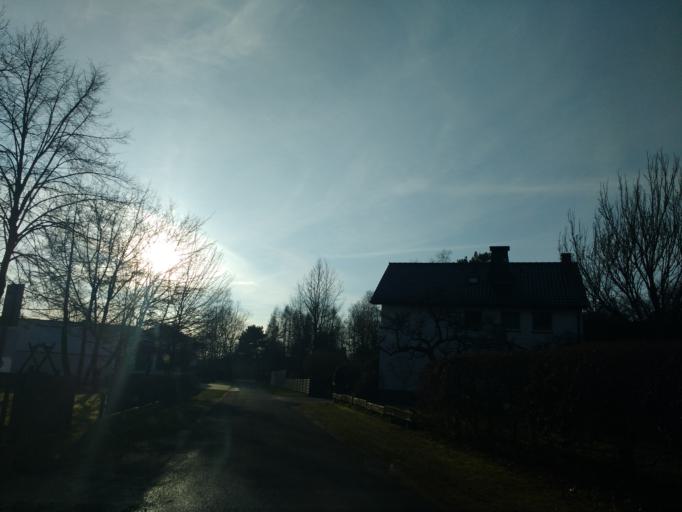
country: DE
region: North Rhine-Westphalia
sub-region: Regierungsbezirk Detmold
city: Hovelhof
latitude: 51.8434
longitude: 8.6522
